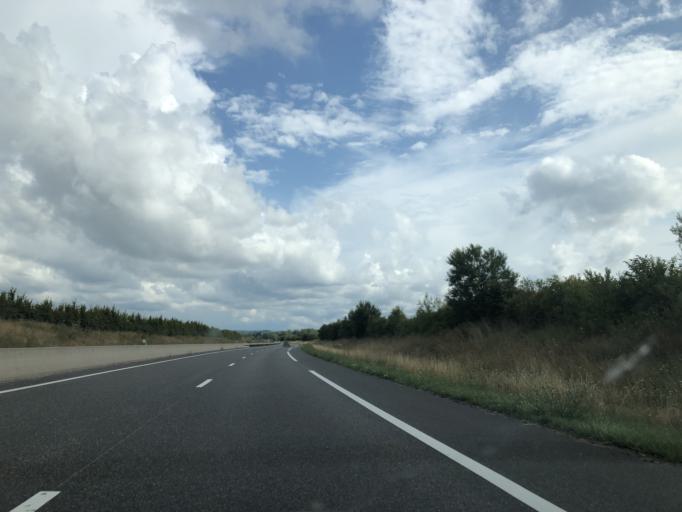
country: FR
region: Lorraine
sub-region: Departement de Meurthe-et-Moselle
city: Baccarat
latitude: 48.4887
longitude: 6.7077
